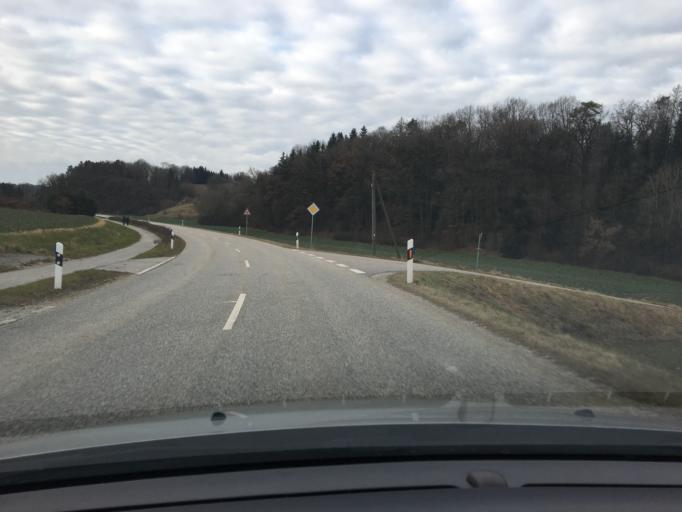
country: DE
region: Bavaria
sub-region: Lower Bavaria
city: Kumhausen
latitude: 48.5000
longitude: 12.1782
